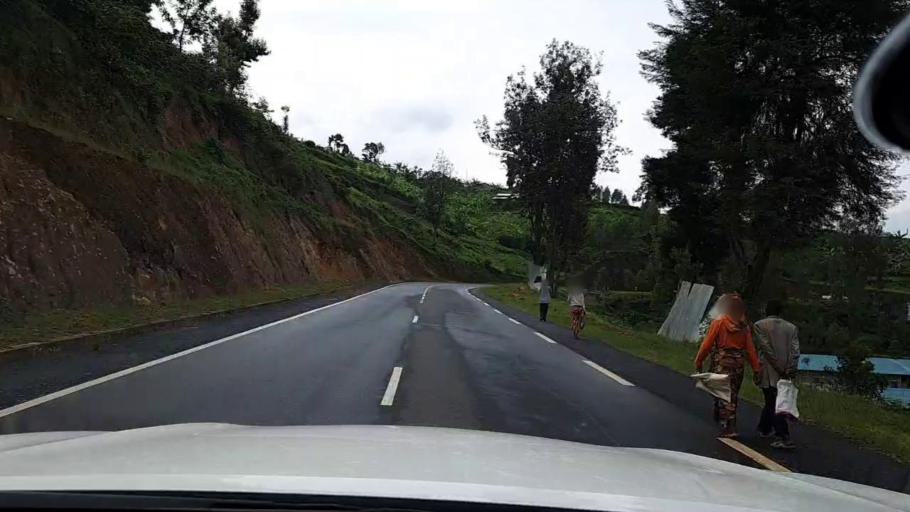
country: RW
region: Western Province
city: Kibuye
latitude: -2.1566
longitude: 29.2968
